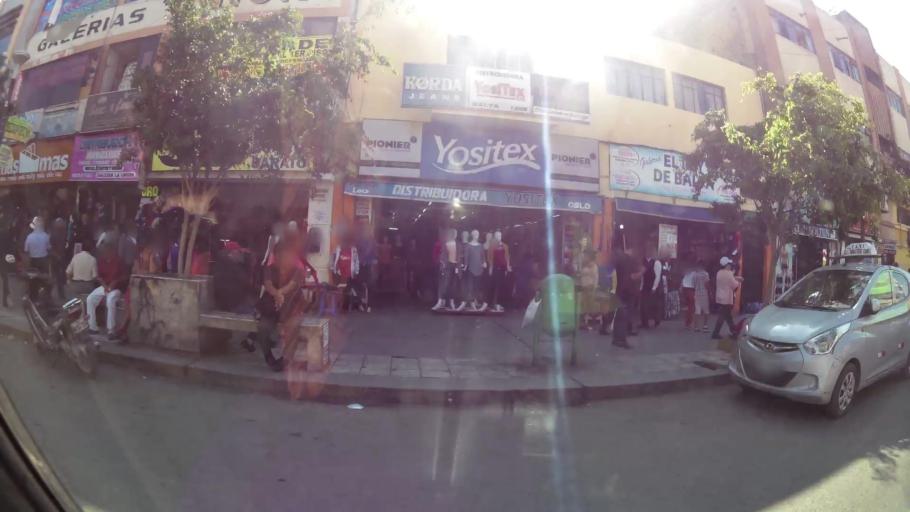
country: PE
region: Lambayeque
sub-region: Provincia de Chiclayo
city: Santa Rosa
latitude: -6.7671
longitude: -79.8380
